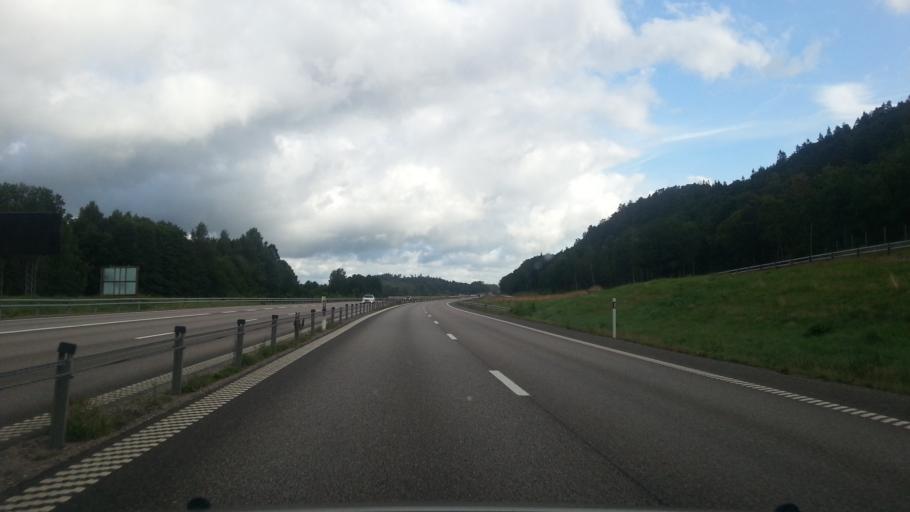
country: SE
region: Vaestra Goetaland
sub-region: Lilla Edets Kommun
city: Lilla Edet
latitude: 58.1488
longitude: 12.1348
